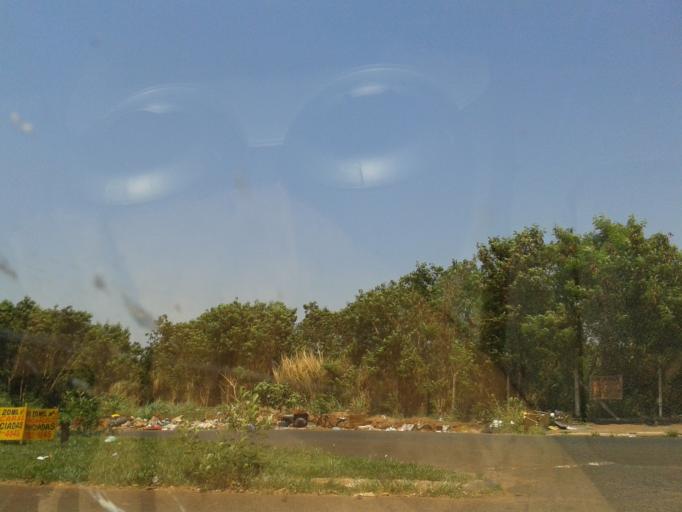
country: BR
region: Minas Gerais
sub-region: Uberlandia
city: Uberlandia
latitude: -18.9604
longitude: -48.3068
